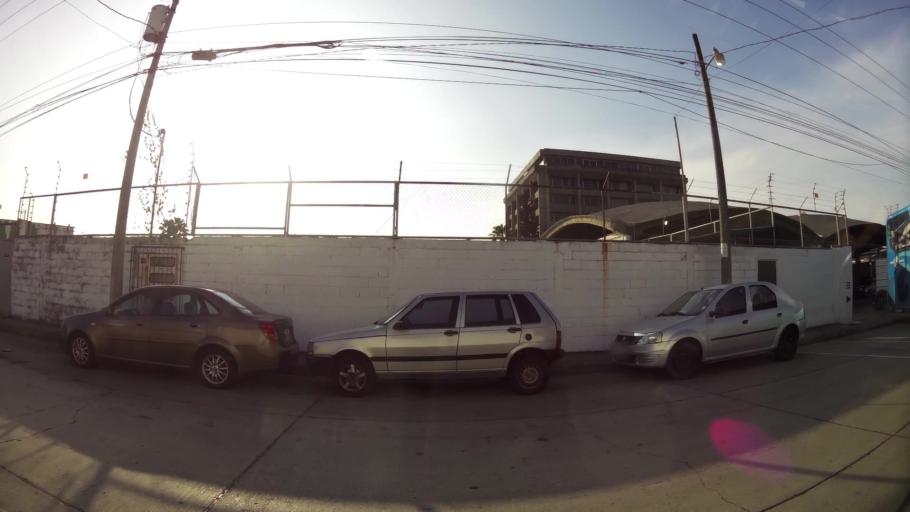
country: EC
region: Guayas
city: Eloy Alfaro
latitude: -2.1661
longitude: -79.8933
